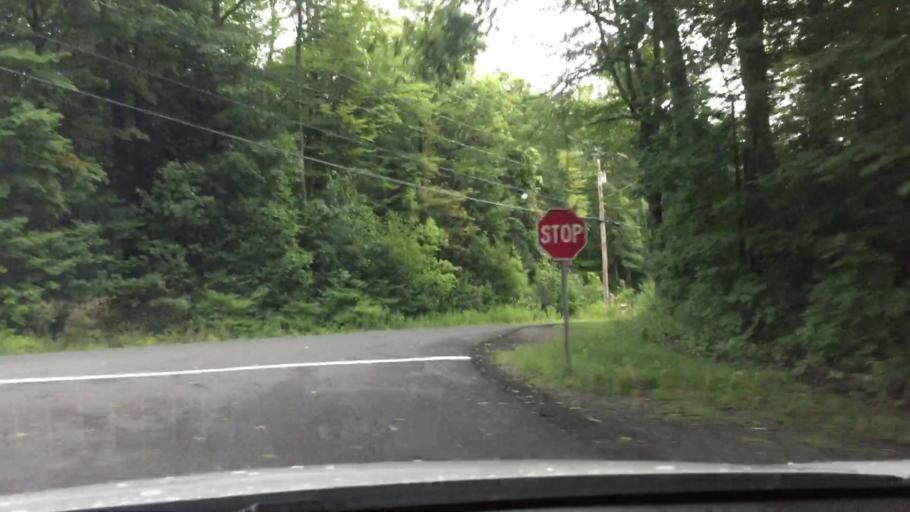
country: US
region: Massachusetts
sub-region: Berkshire County
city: Otis
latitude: 42.1713
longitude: -73.0541
